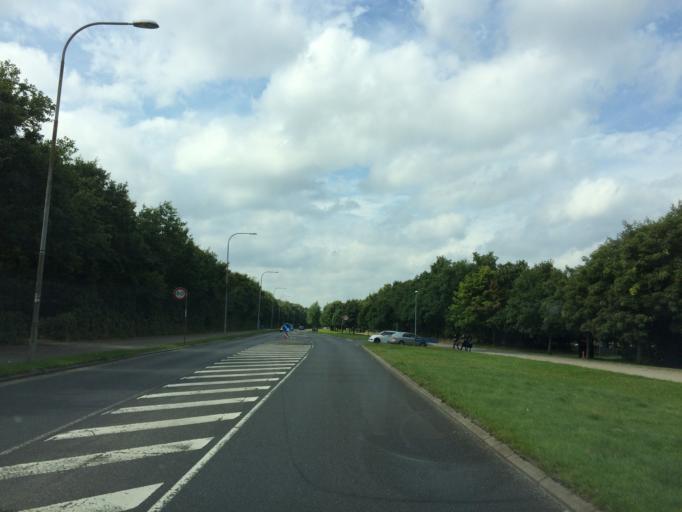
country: DK
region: Central Jutland
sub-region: Holstebro Kommune
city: Holstebro
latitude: 56.3752
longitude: 8.6036
